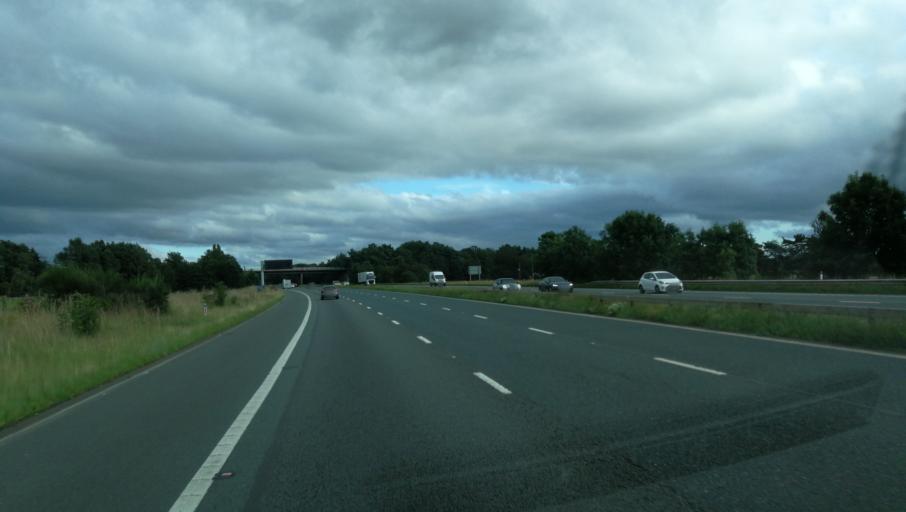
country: GB
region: England
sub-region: Cumbria
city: Scotby
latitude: 54.9153
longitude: -2.9032
